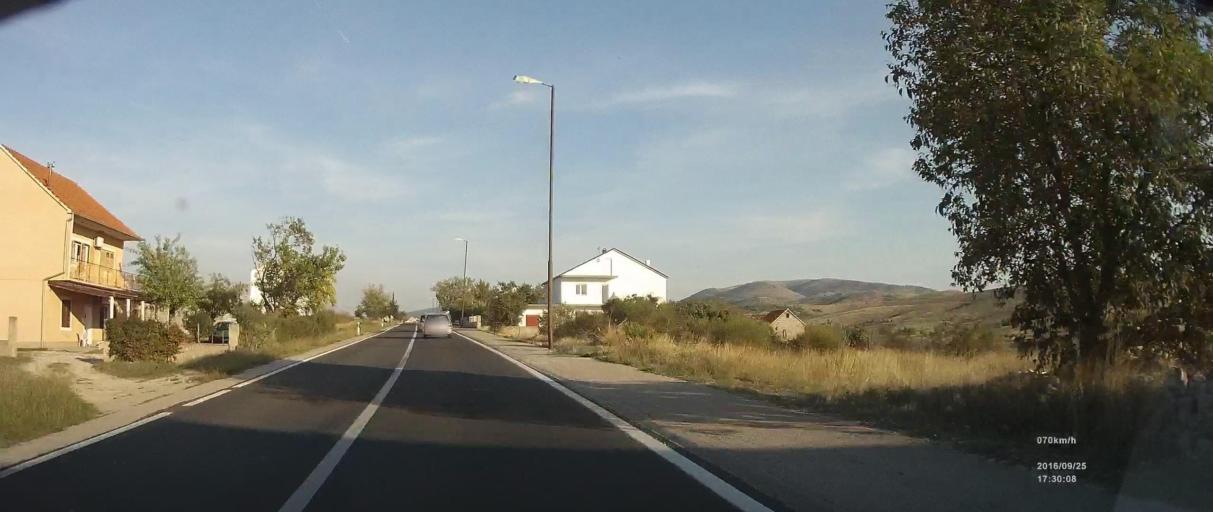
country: HR
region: Sibensko-Kniniska
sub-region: Grad Sibenik
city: Brodarica
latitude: 43.6820
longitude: 15.9736
